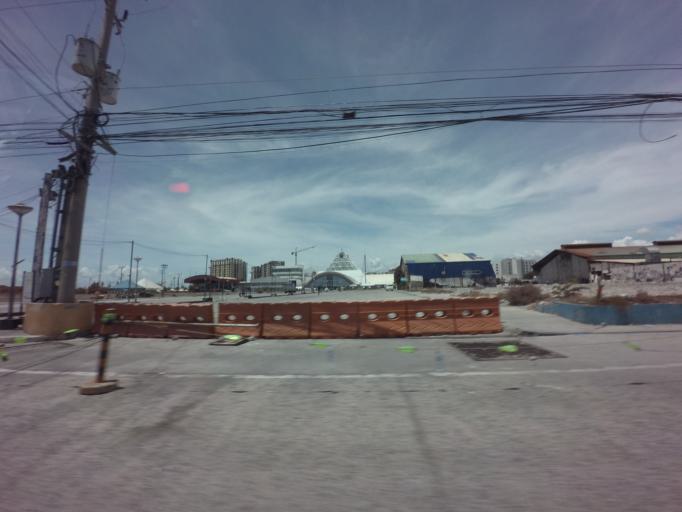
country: PH
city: Sambayanihan People's Village
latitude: 14.4921
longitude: 120.9938
